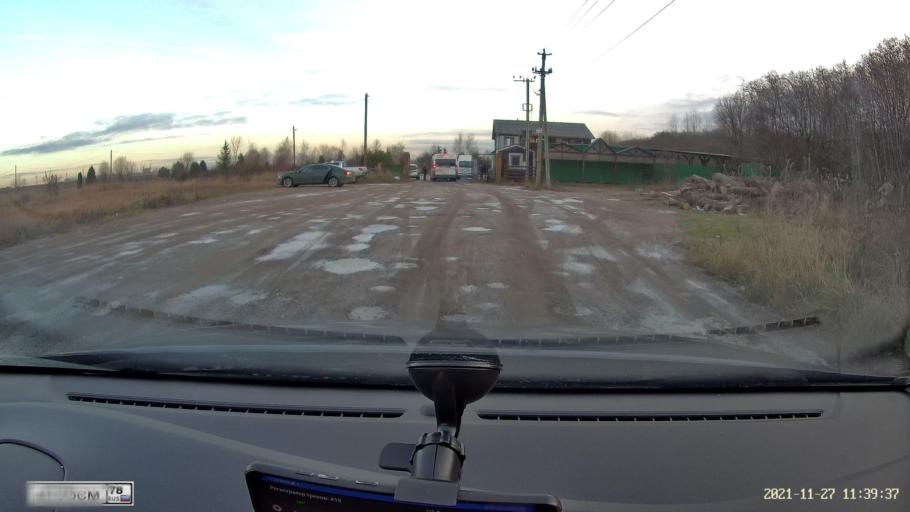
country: RU
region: Leningrad
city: Russko-Vysotskoye
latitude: 59.6870
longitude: 30.0037
